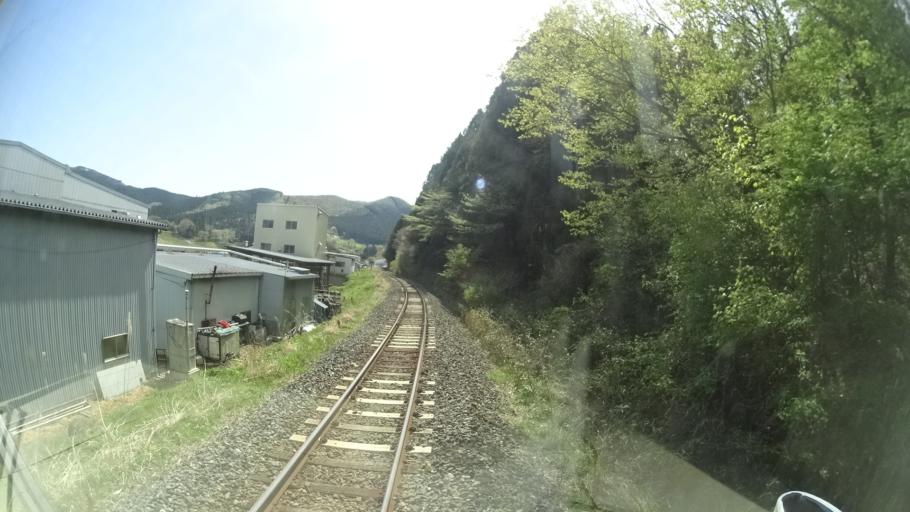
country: JP
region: Iwate
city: Ofunato
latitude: 38.9358
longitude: 141.4617
